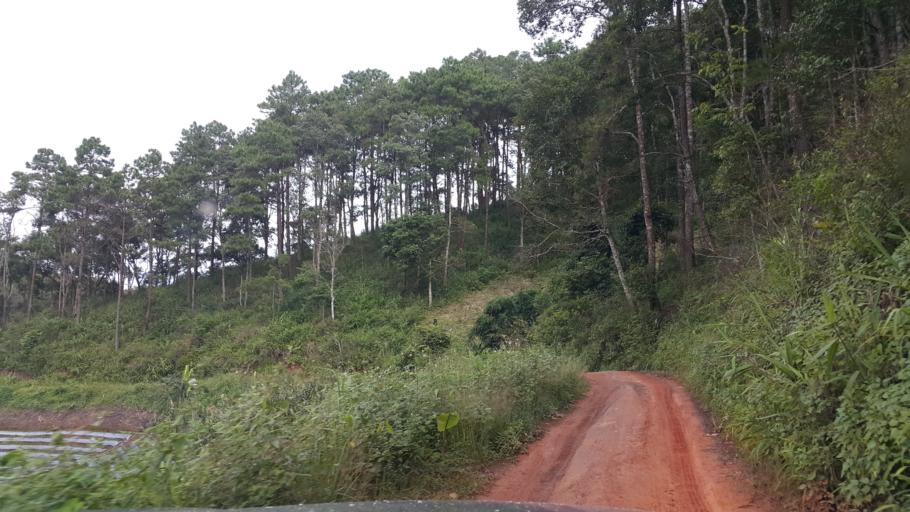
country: TH
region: Chiang Mai
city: Samoeng
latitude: 18.8762
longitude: 98.5082
